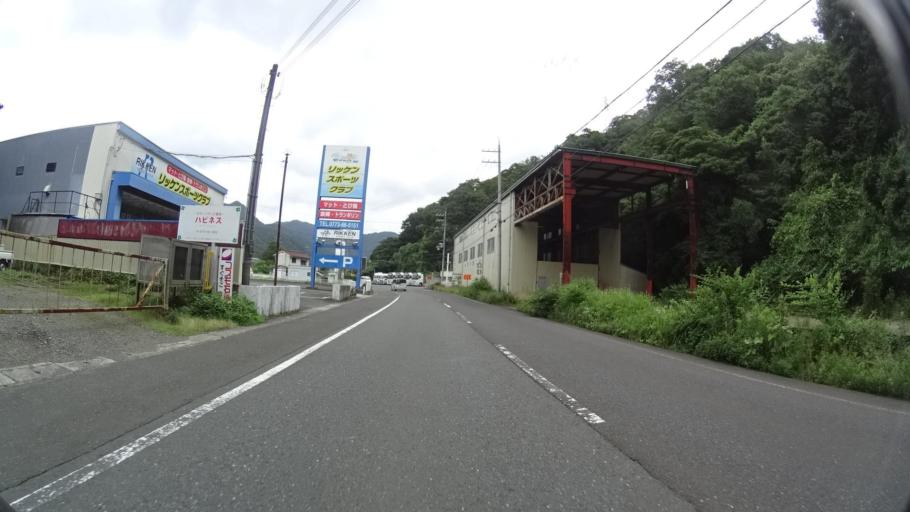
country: JP
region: Kyoto
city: Maizuru
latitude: 35.4948
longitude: 135.3939
